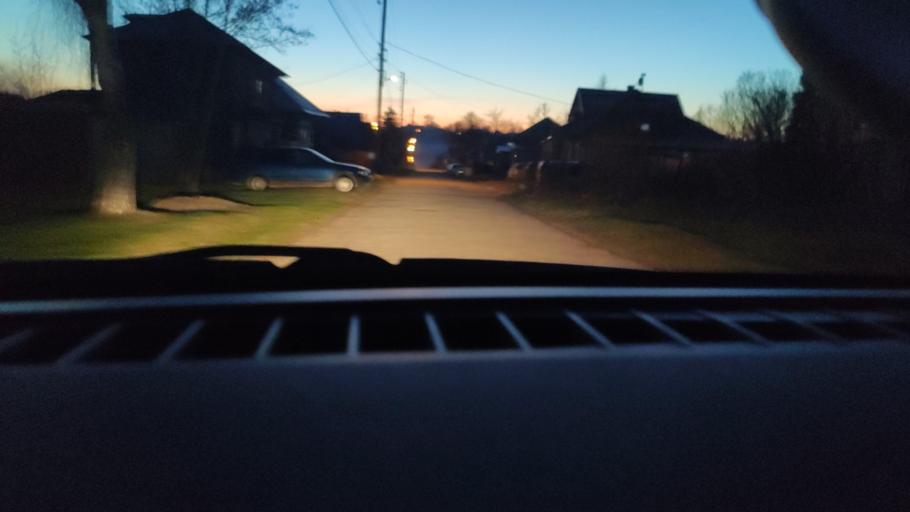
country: RU
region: Perm
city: Perm
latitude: 58.0396
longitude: 56.3372
